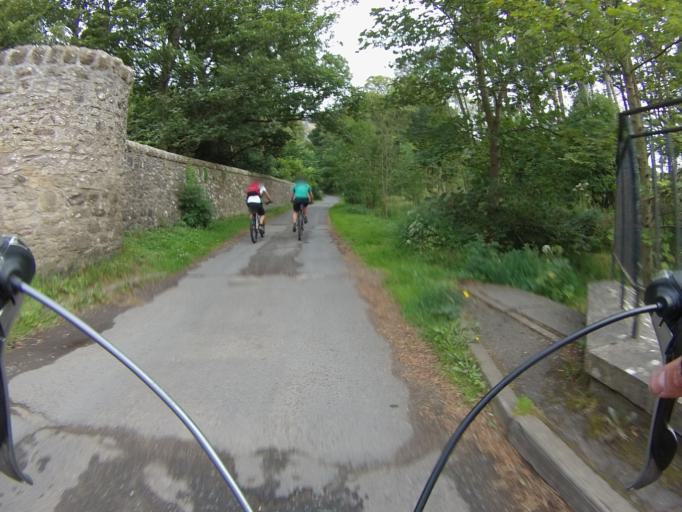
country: GB
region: Scotland
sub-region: Edinburgh
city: Colinton
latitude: 55.8967
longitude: -3.2617
